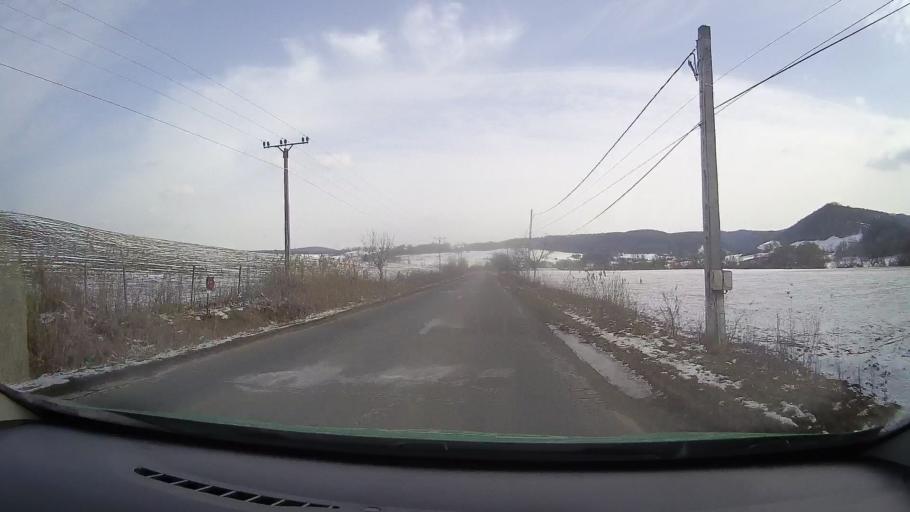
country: RO
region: Mures
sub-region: Comuna Apold
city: Saes
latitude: 46.1431
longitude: 24.7824
